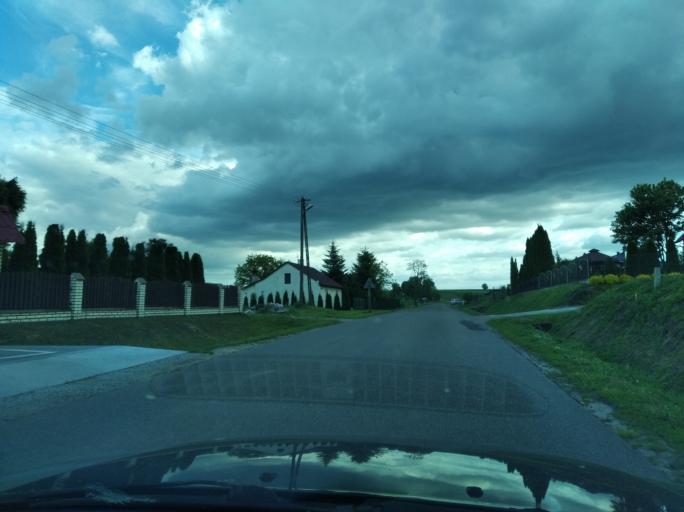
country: PL
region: Subcarpathian Voivodeship
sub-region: Powiat jaroslawski
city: Rokietnica
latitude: 49.9378
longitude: 22.6664
